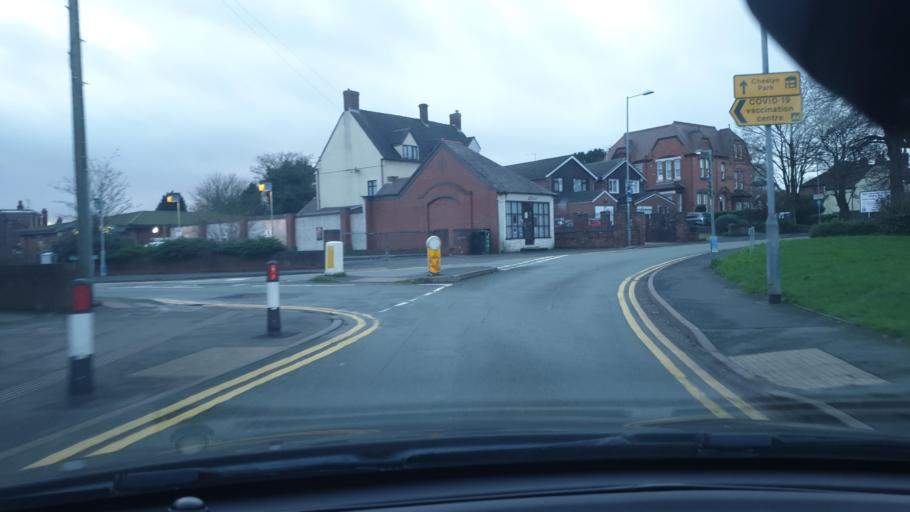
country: GB
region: England
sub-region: Staffordshire
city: Great Wyrley
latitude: 52.6601
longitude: -2.0318
